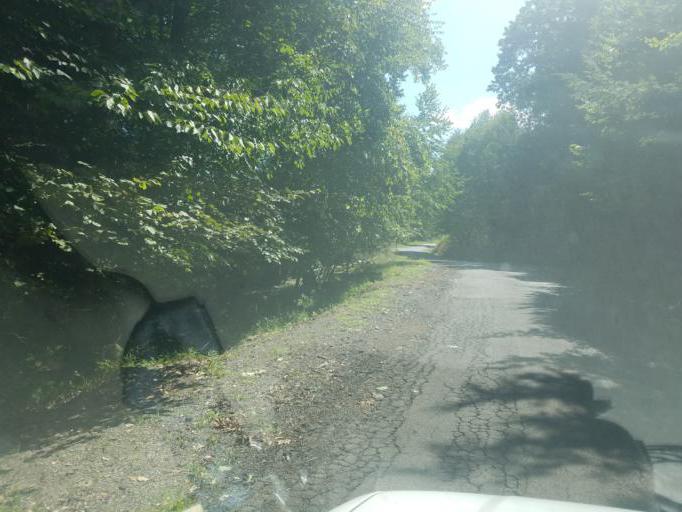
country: US
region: Pennsylvania
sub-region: Clarion County
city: Marianne
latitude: 41.1904
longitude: -79.4385
